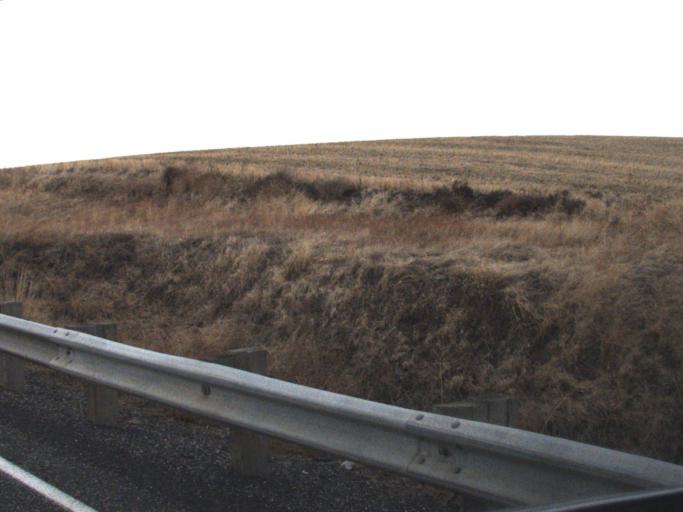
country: US
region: Washington
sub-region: Garfield County
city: Pomeroy
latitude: 46.4362
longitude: -117.4196
